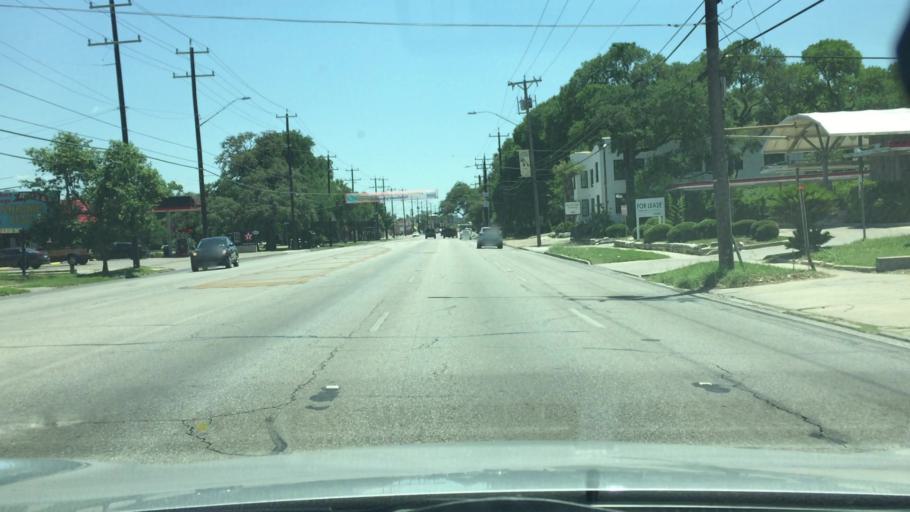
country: US
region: Texas
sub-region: Bexar County
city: Terrell Hills
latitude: 29.4593
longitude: -98.4681
